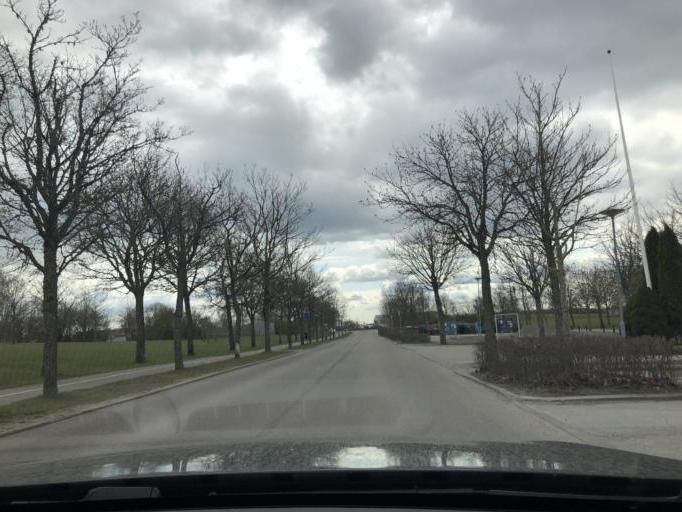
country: SE
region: Uppsala
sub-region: Uppsala Kommun
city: Uppsala
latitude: 59.8210
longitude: 17.6565
